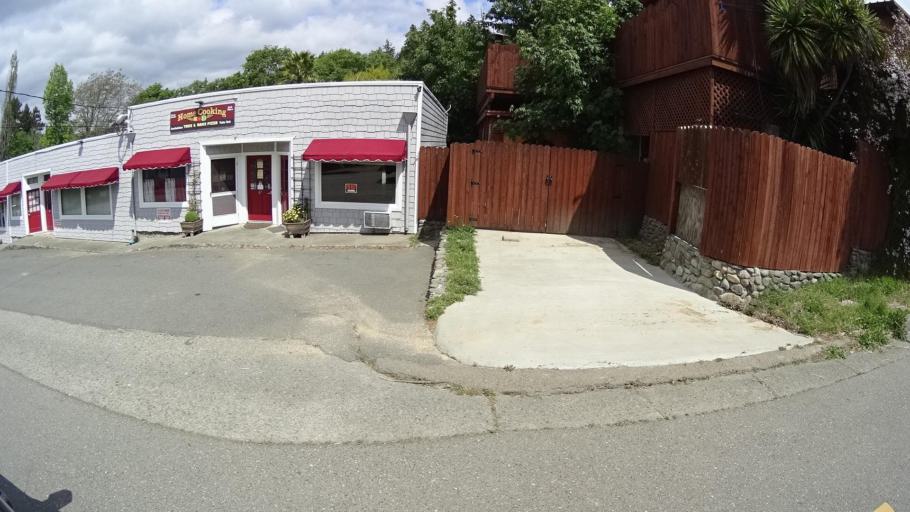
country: US
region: California
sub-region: Humboldt County
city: Redway
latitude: 40.1209
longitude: -123.8245
